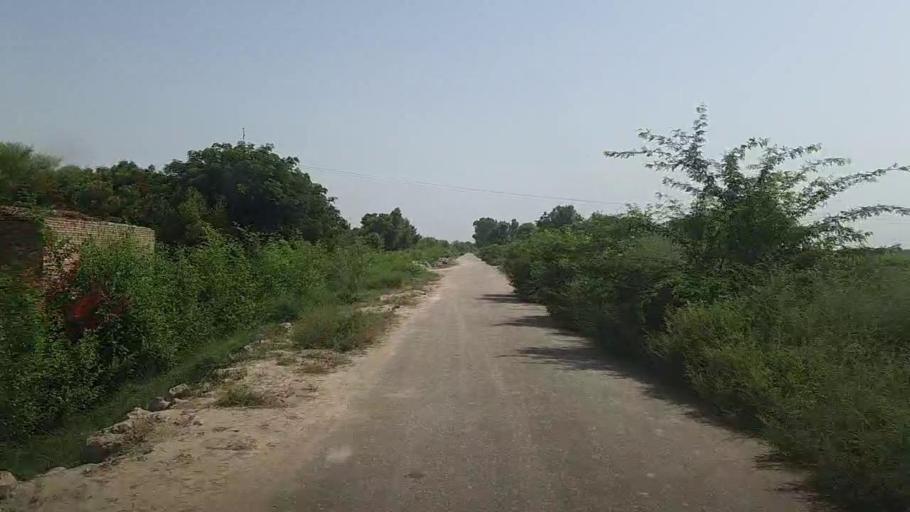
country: PK
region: Sindh
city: Pad Idan
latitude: 26.8003
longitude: 68.3320
